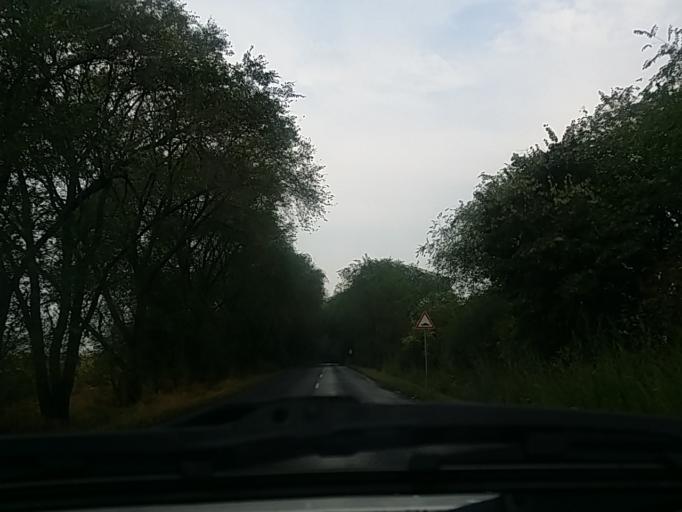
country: HU
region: Pest
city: Telki
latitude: 47.5348
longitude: 18.7768
